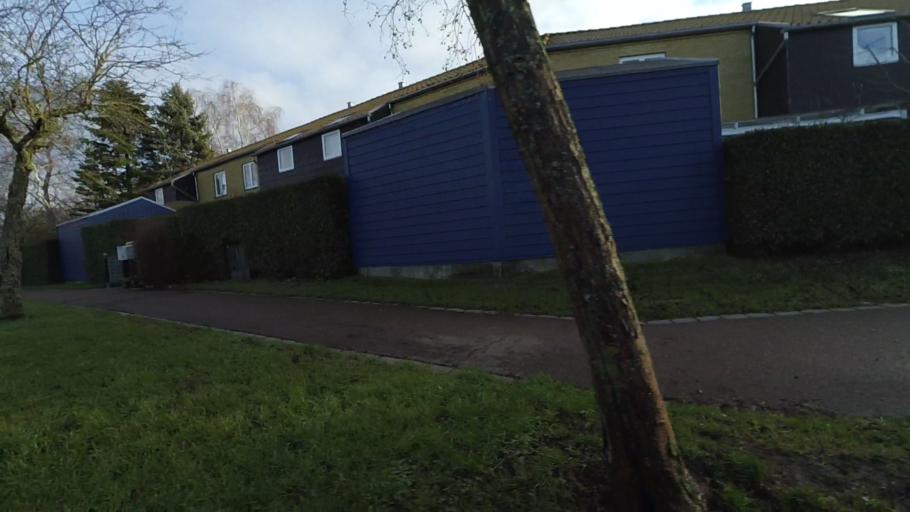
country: DK
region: Central Jutland
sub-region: Arhus Kommune
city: Marslet
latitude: 56.1080
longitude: 10.1715
